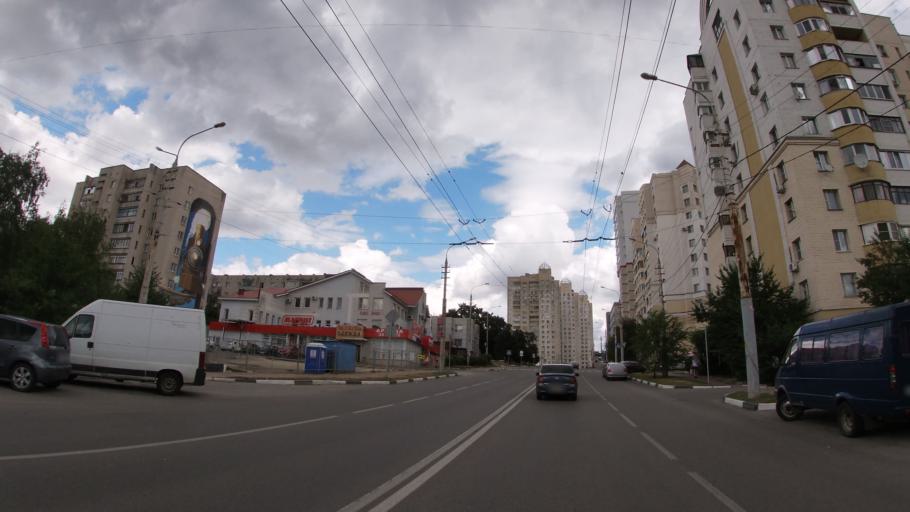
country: RU
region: Belgorod
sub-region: Belgorodskiy Rayon
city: Belgorod
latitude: 50.5983
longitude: 36.6069
